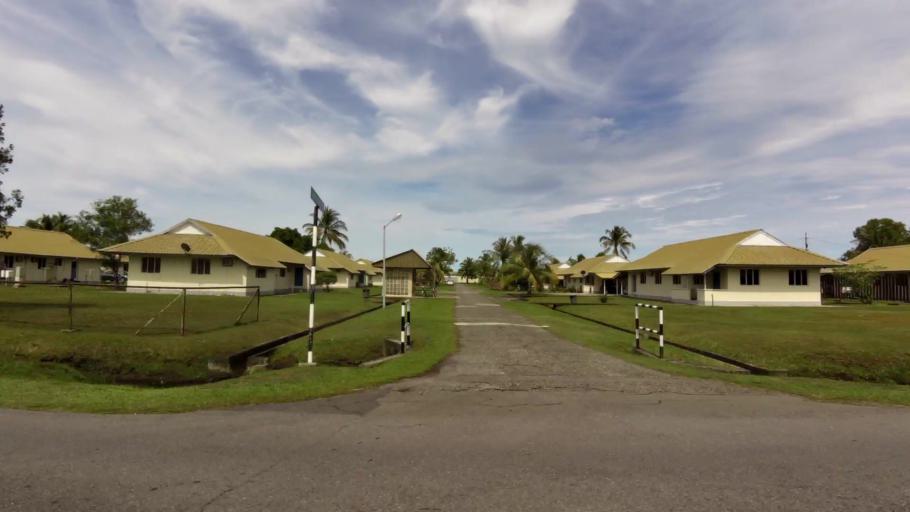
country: BN
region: Belait
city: Seria
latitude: 4.6056
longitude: 114.3169
